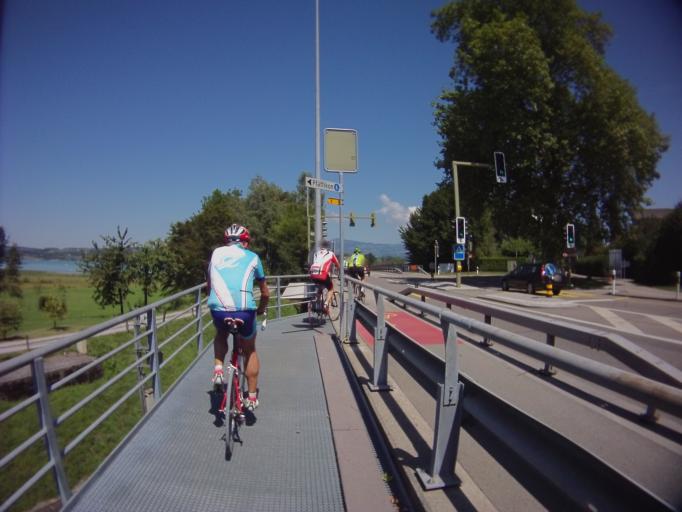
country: CH
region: Saint Gallen
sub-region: Wahlkreis See-Gaster
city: Rapperswil
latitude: 47.2133
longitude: 8.7994
